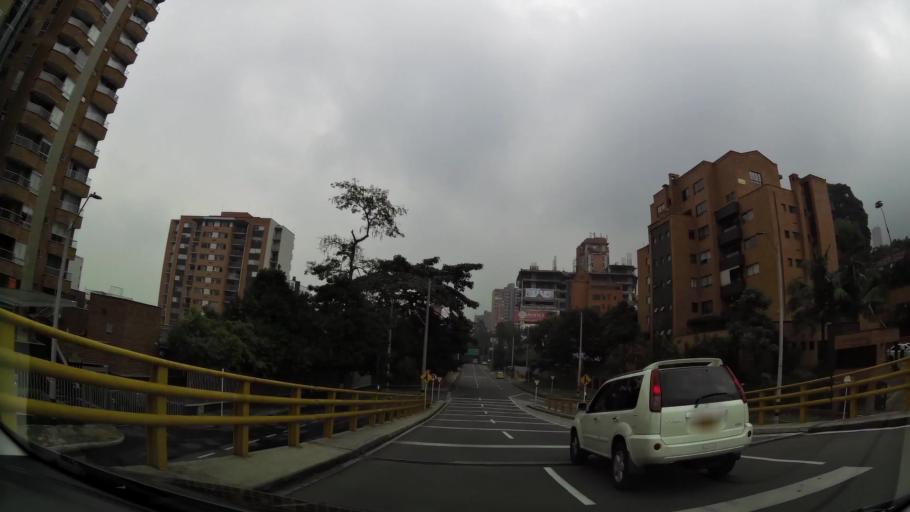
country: CO
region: Antioquia
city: Envigado
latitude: 6.1877
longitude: -75.5615
